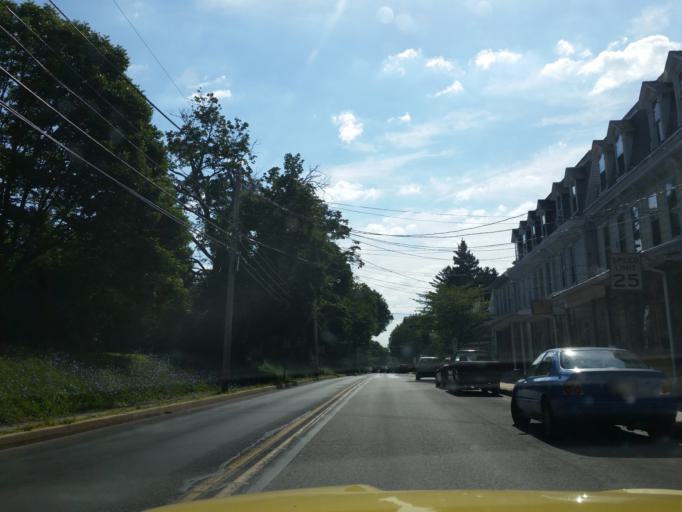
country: US
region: Pennsylvania
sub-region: Lebanon County
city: Lebanon
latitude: 40.3501
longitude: -76.4187
